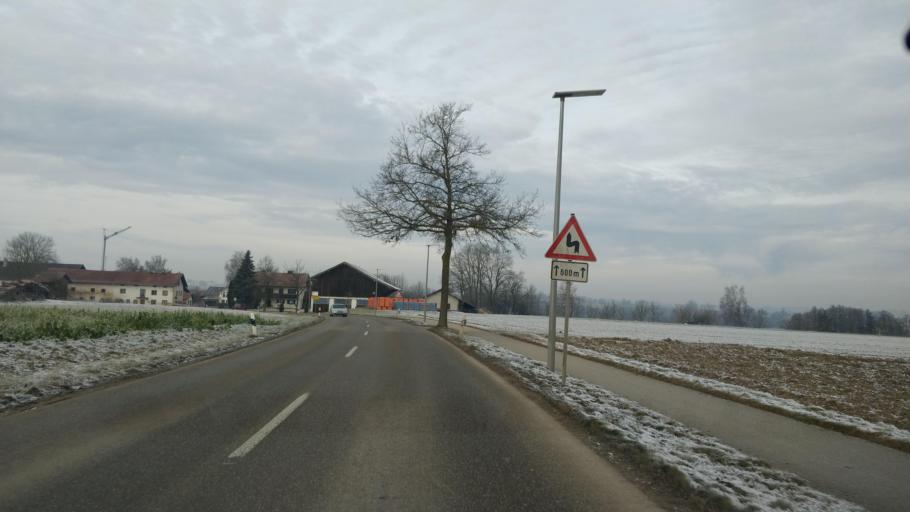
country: DE
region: Bavaria
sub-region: Upper Bavaria
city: Obertaufkirchen
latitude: 48.2683
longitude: 12.2724
